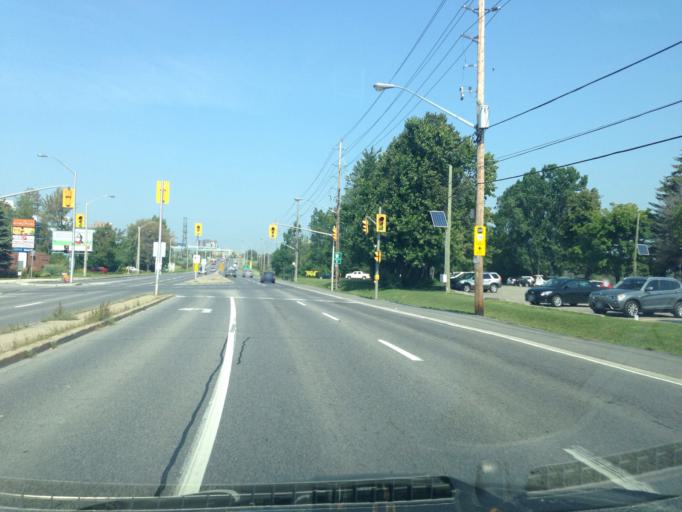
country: CA
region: Ontario
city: Ottawa
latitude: 45.4268
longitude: -75.5999
